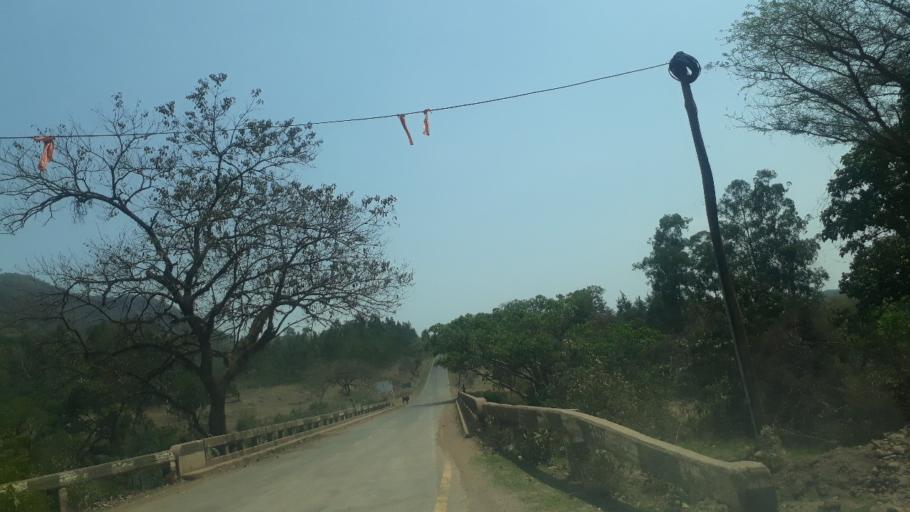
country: ET
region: Oromiya
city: Agaro
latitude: 8.0442
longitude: 36.4736
